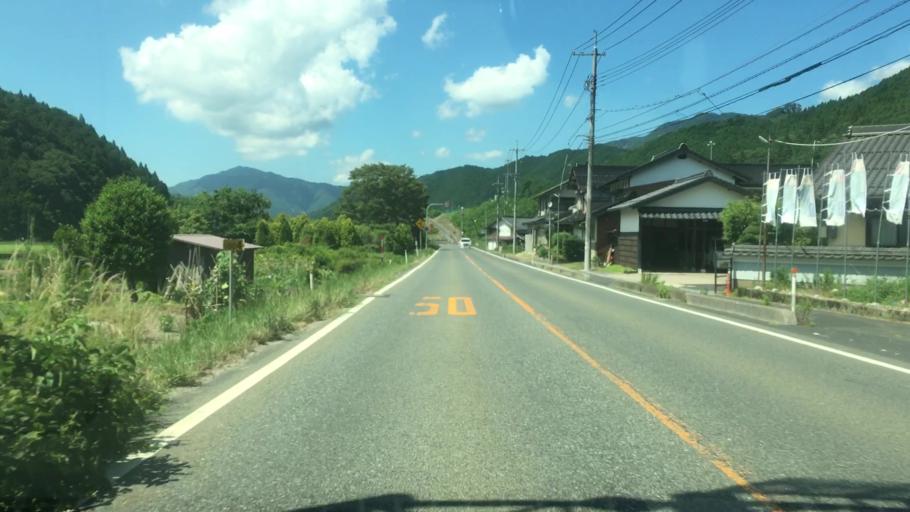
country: JP
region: Tottori
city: Tottori
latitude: 35.2418
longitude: 134.2293
